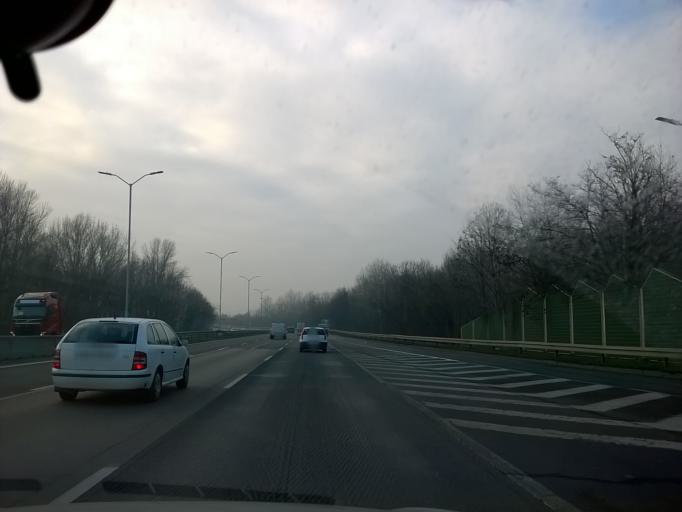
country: PL
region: Silesian Voivodeship
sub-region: Swietochlowice
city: Swietochlowice
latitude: 50.2969
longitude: 18.9128
